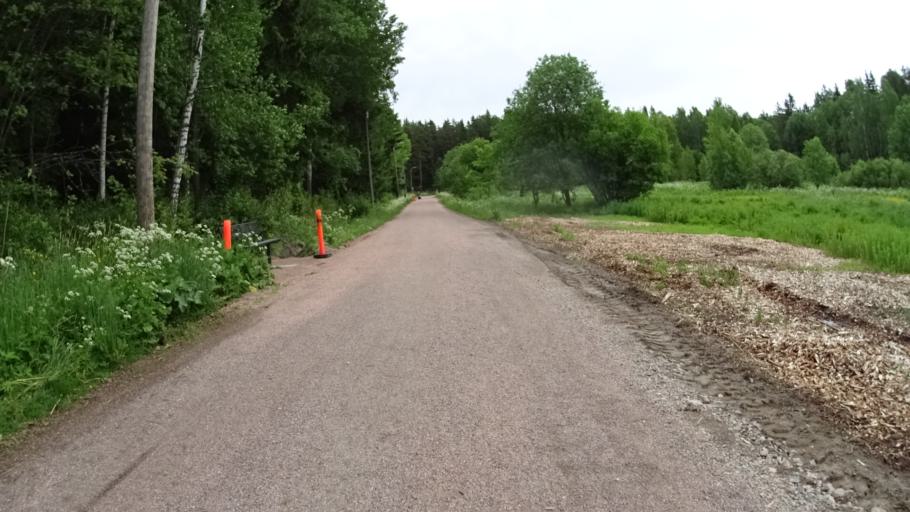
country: FI
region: Uusimaa
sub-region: Helsinki
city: Kilo
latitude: 60.2748
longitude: 24.8232
